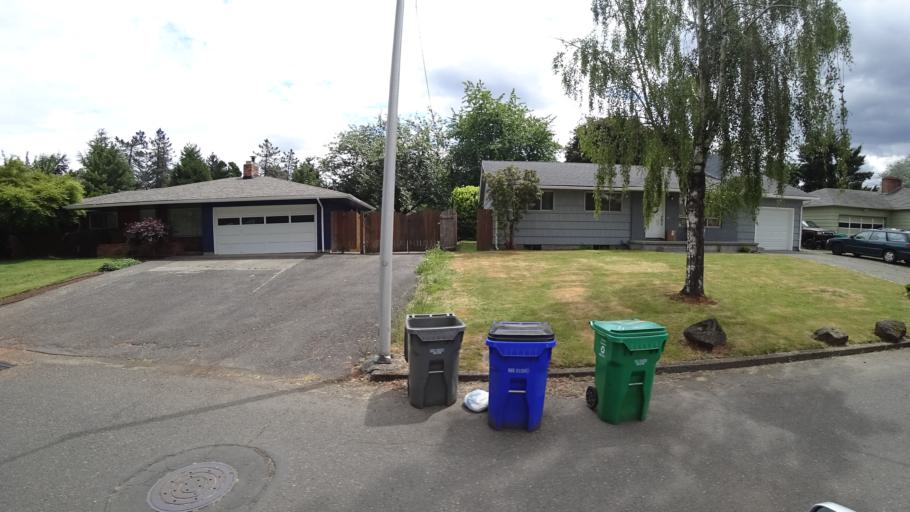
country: US
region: Oregon
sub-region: Clackamas County
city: Happy Valley
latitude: 45.5005
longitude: -122.5153
